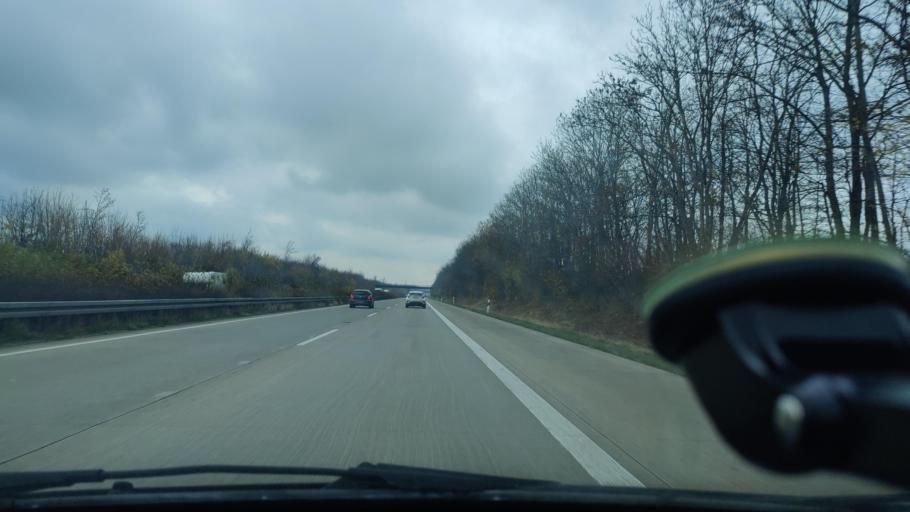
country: DE
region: North Rhine-Westphalia
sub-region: Regierungsbezirk Arnsberg
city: Anrochte
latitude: 51.5857
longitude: 8.3461
